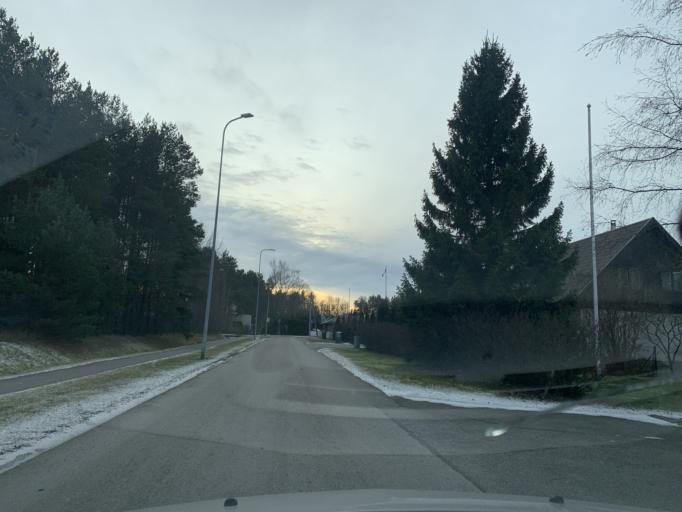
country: EE
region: Harju
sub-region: Harku vald
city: Tabasalu
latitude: 59.4402
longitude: 24.5775
